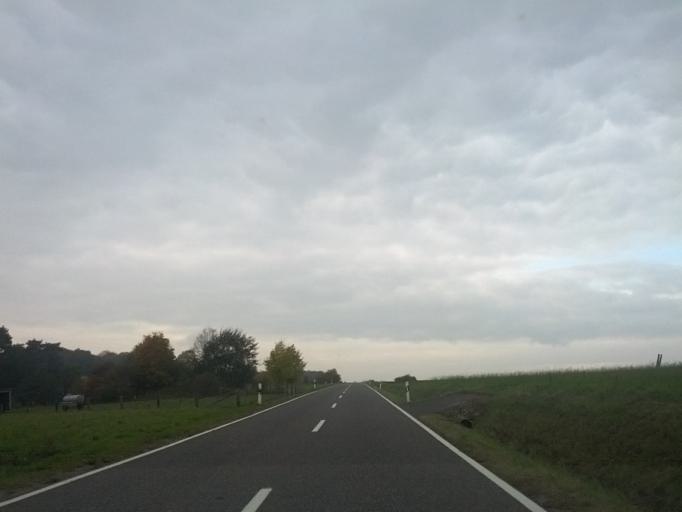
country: DE
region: Hesse
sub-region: Regierungsbezirk Kassel
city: Herleshausen
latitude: 51.0369
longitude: 10.1751
